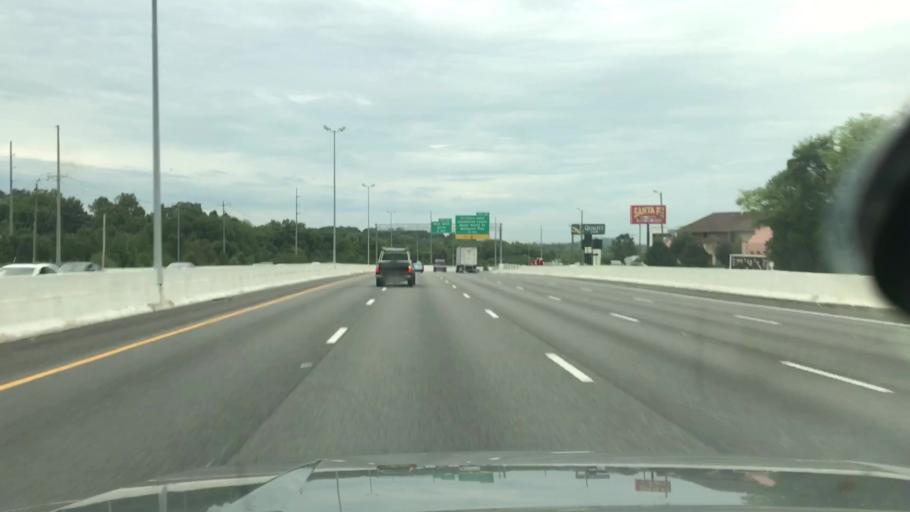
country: US
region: Tennessee
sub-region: Davidson County
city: Lakewood
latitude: 36.2268
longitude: -86.6964
